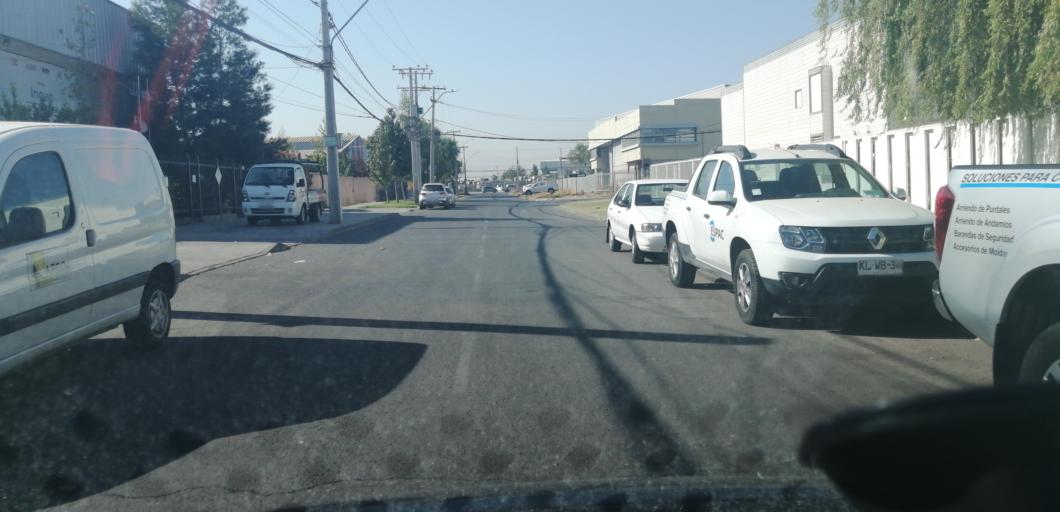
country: CL
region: Santiago Metropolitan
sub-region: Provincia de Santiago
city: Lo Prado
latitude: -33.3823
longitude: -70.7782
